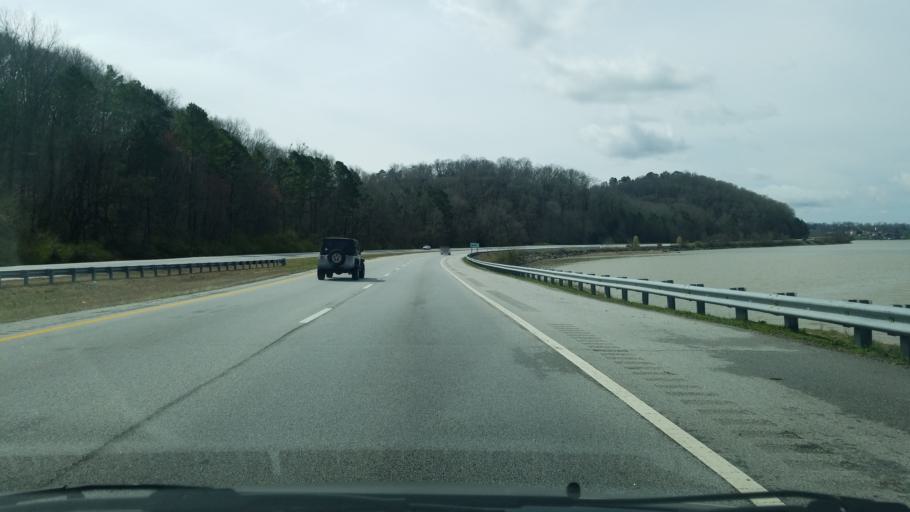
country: US
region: Tennessee
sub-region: Hamilton County
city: Harrison
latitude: 35.1484
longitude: -85.1097
